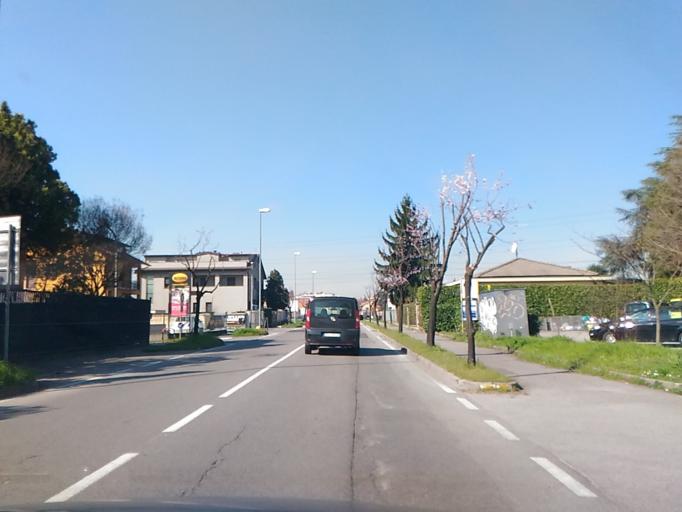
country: IT
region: Lombardy
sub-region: Provincia di Monza e Brianza
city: Brugherio
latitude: 45.5465
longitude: 9.3078
